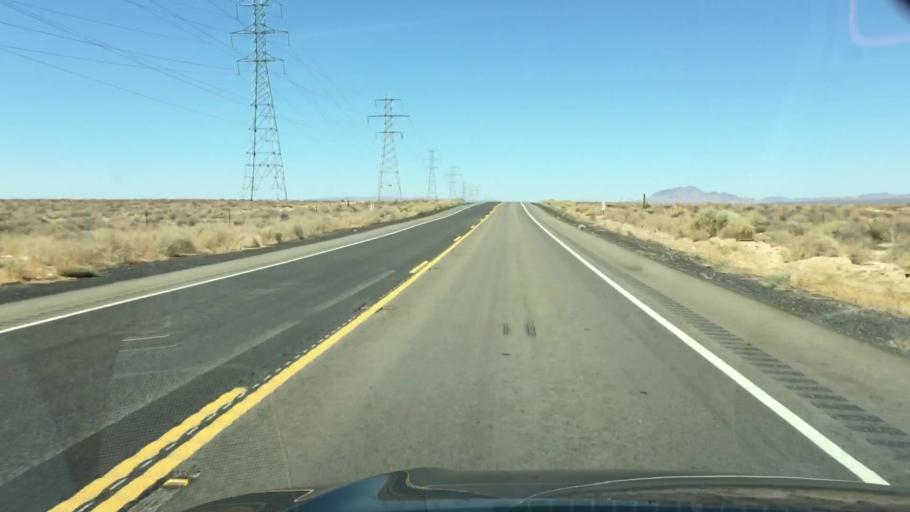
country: US
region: California
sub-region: Kern County
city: Boron
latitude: 35.1042
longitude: -117.5727
